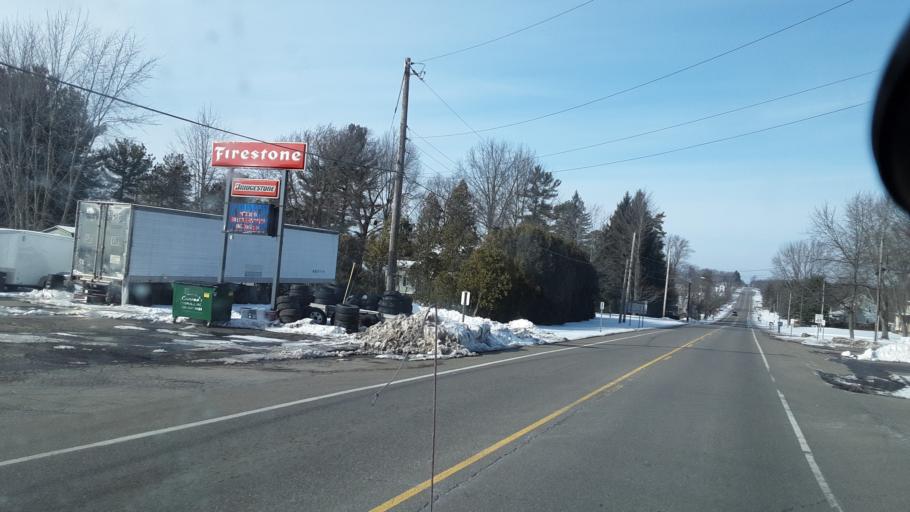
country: US
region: Ohio
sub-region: Stark County
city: Alliance
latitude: 41.0239
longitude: -81.1480
